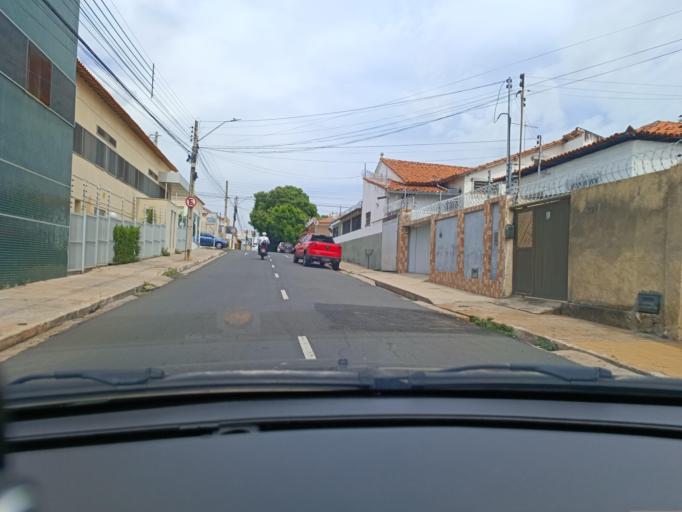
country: BR
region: Piaui
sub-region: Teresina
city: Teresina
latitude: -5.0930
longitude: -42.8101
